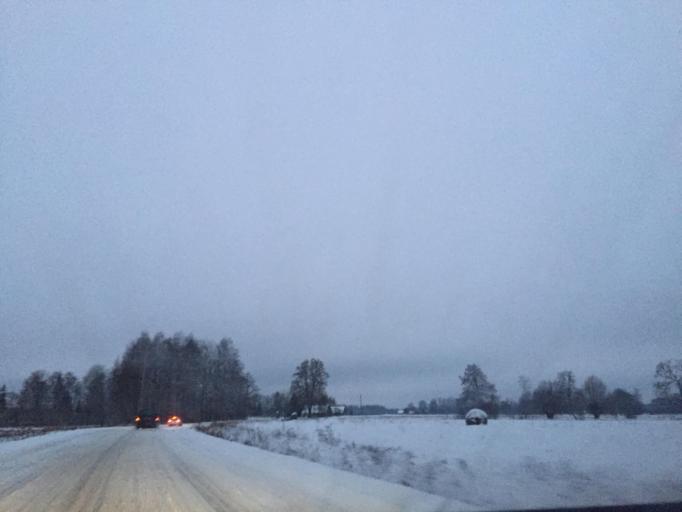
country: LV
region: Beverina
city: Murmuiza
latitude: 57.4062
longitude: 25.5294
